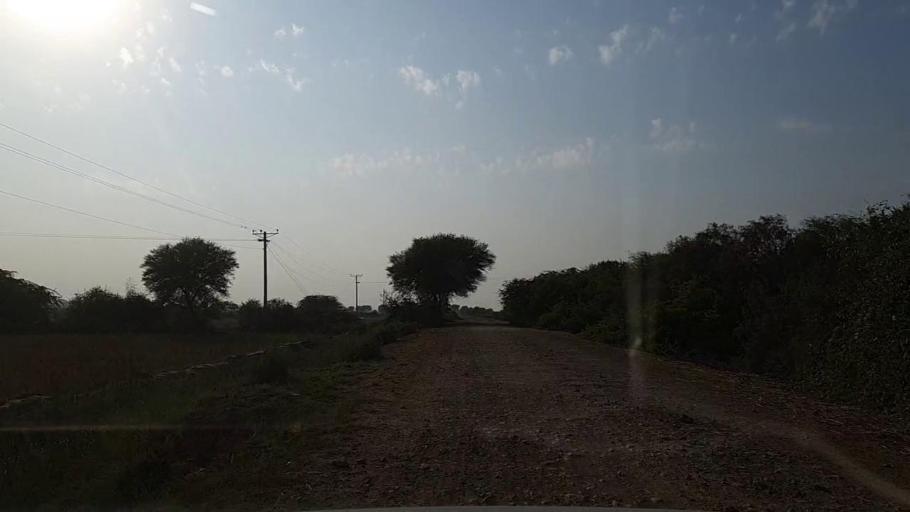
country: PK
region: Sindh
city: Mirpur Batoro
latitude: 24.7900
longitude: 68.2620
